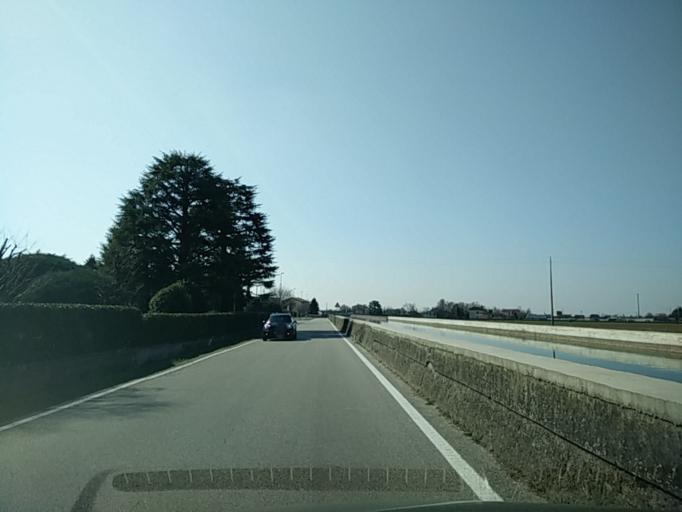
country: IT
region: Veneto
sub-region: Provincia di Treviso
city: Crocetta-Nogare
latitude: 45.8150
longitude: 12.0224
